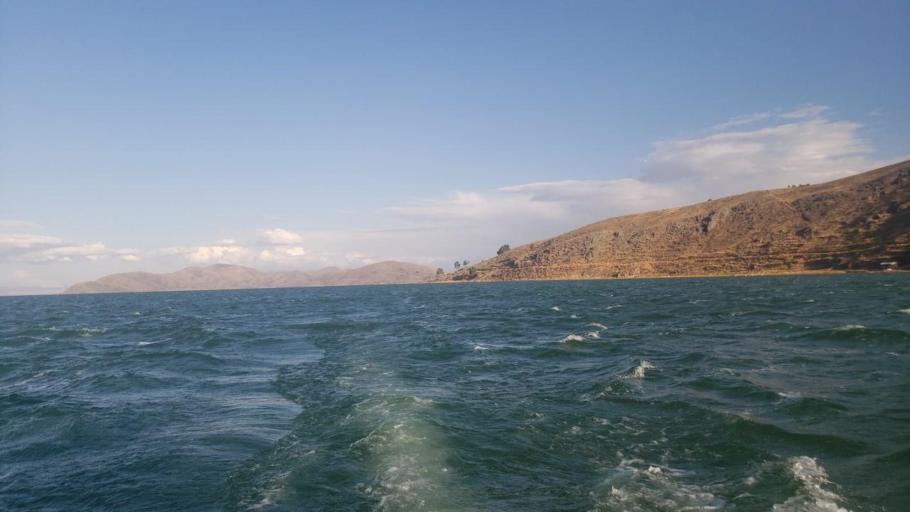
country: BO
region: La Paz
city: San Pablo
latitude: -16.2926
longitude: -68.7596
